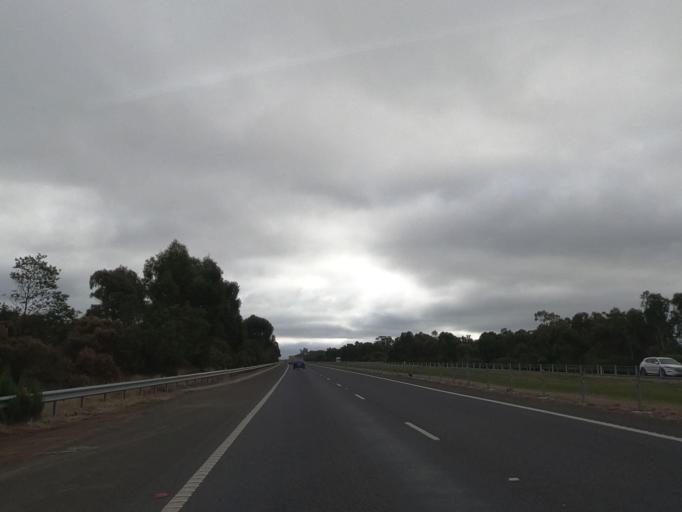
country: AU
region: Victoria
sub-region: Mount Alexander
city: Castlemaine
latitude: -37.0718
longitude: 144.3124
